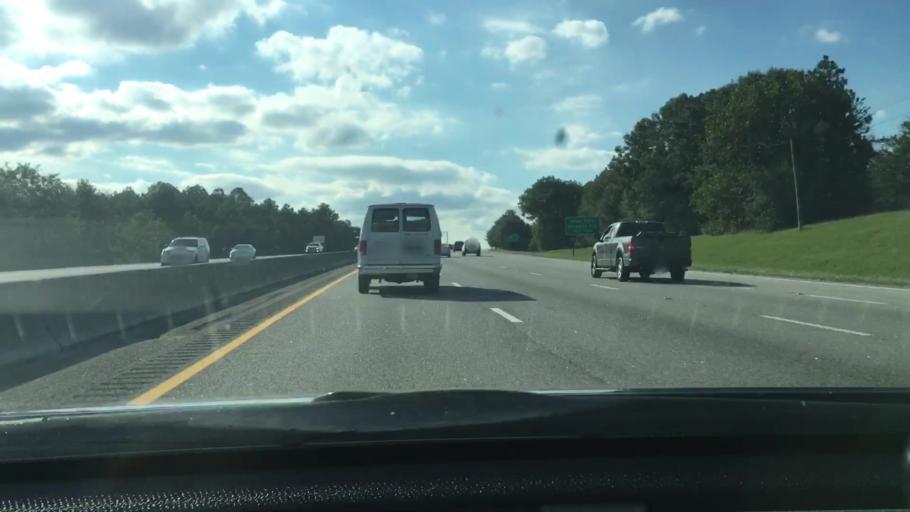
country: US
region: South Carolina
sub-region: Richland County
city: Dentsville
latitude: 34.0730
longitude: -80.9733
